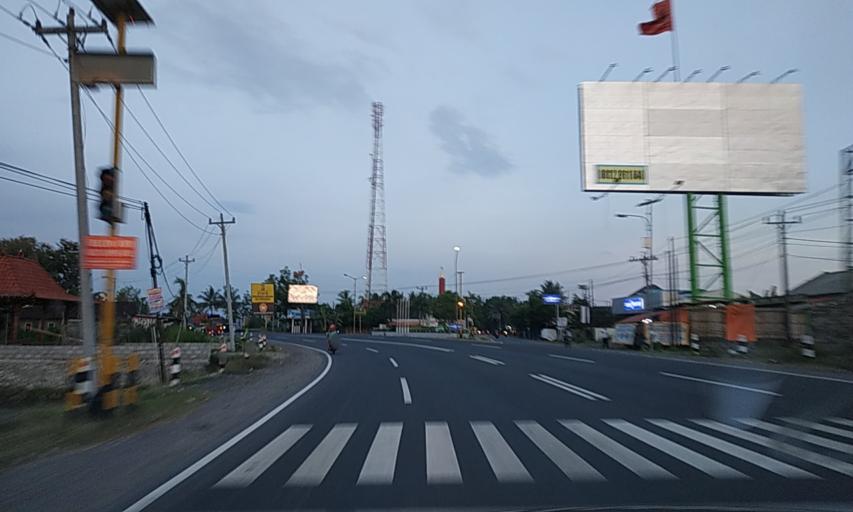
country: ID
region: Daerah Istimewa Yogyakarta
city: Srandakan
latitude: -7.8758
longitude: 110.2049
